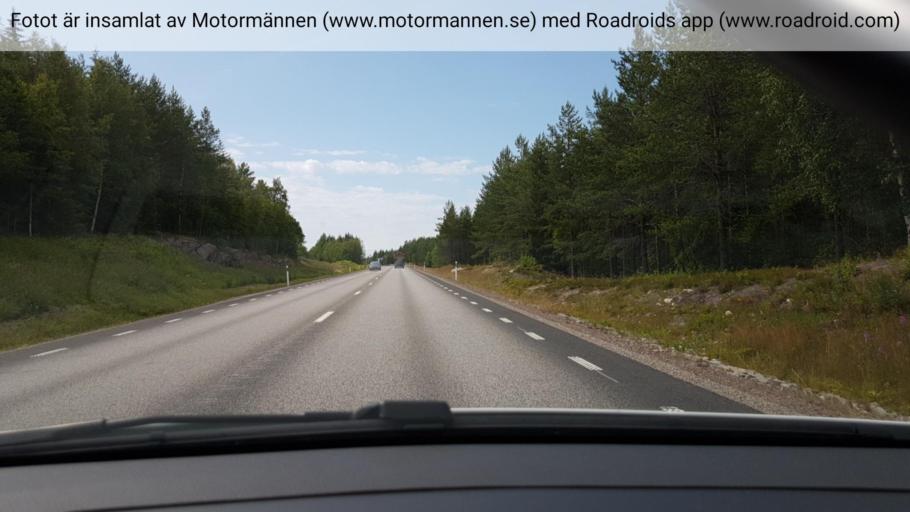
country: SE
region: Dalarna
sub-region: Rattviks Kommun
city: Raettvik
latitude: 60.8427
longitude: 15.1936
